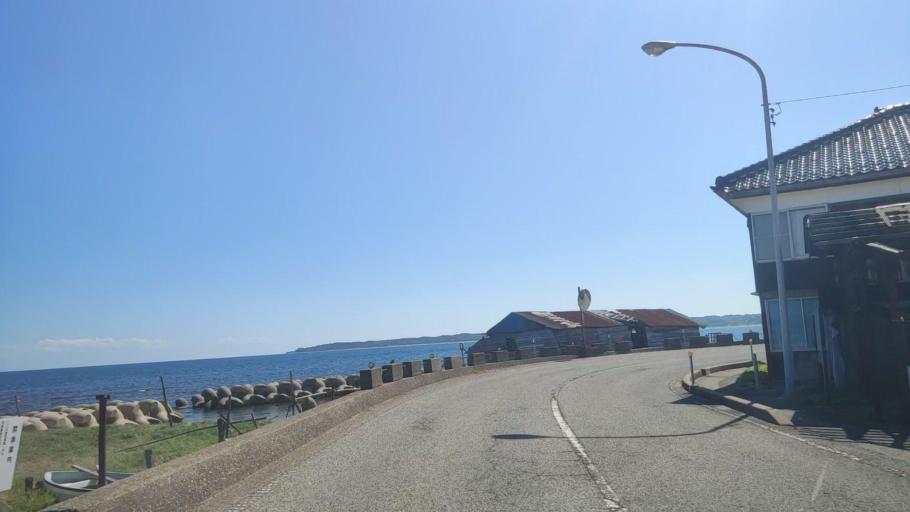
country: JP
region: Toyama
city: Nyuzen
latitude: 37.4974
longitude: 137.3496
